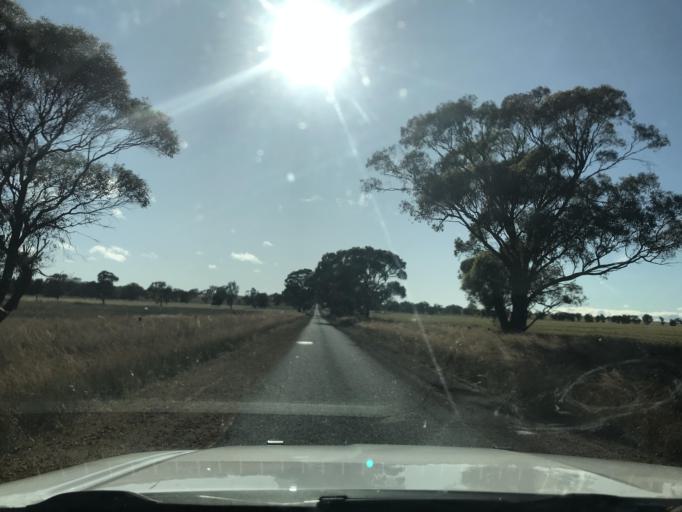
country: AU
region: Victoria
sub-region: Horsham
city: Horsham
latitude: -36.6960
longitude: 141.5858
